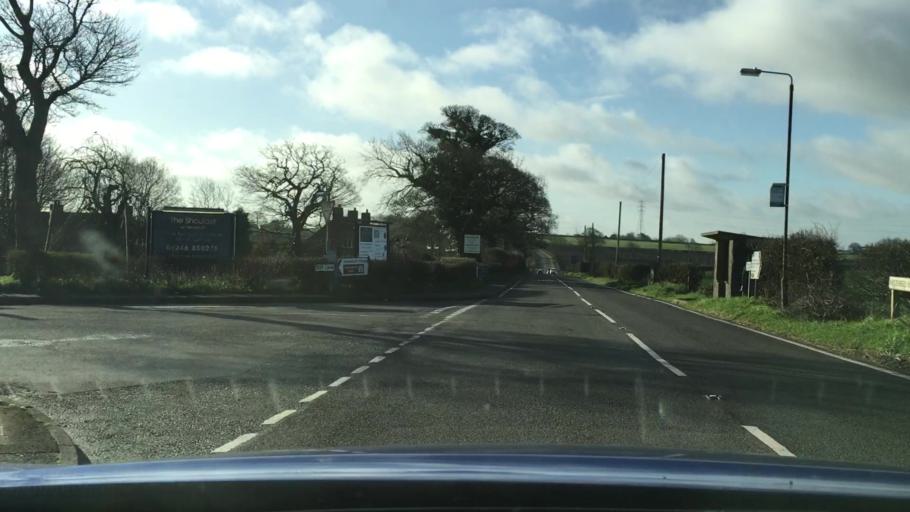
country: GB
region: England
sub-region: Derbyshire
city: Tibshelf
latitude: 53.1619
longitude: -1.3456
